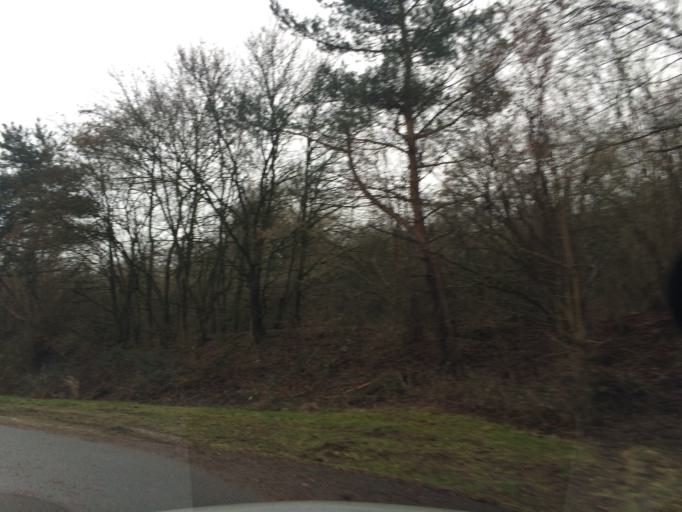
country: DE
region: Hesse
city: Morfelden-Walldorf
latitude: 50.0129
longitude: 8.5950
